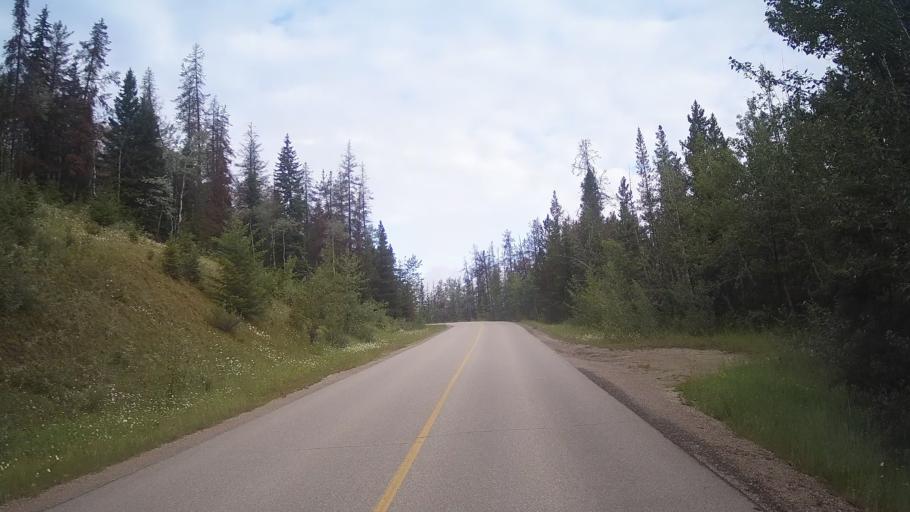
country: CA
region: Alberta
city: Jasper Park Lodge
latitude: 52.8579
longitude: -118.0967
